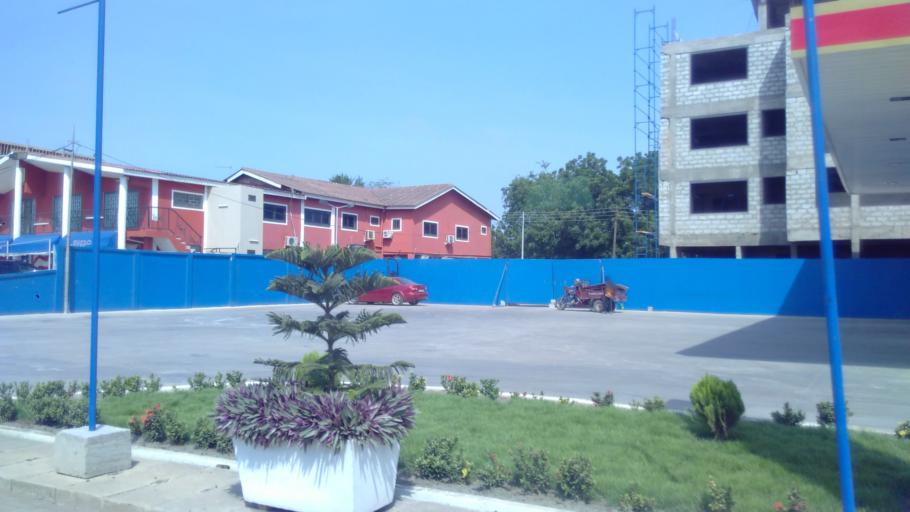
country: GH
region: Greater Accra
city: Nungua
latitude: 5.6167
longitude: -0.0724
